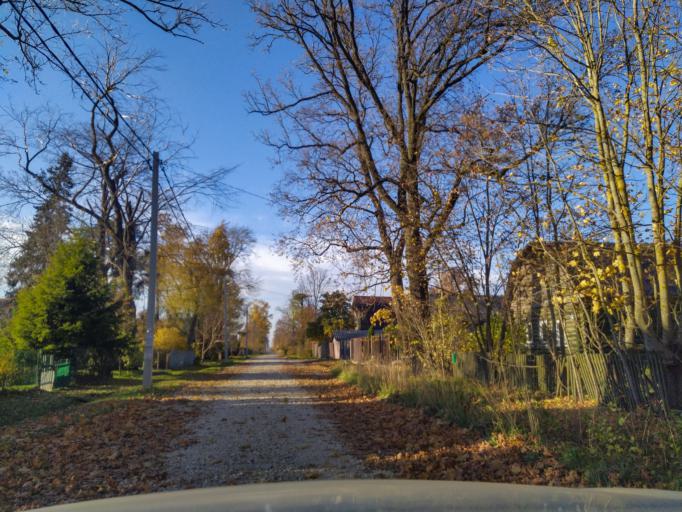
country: RU
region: Leningrad
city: Siverskiy
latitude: 59.3247
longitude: 30.0433
